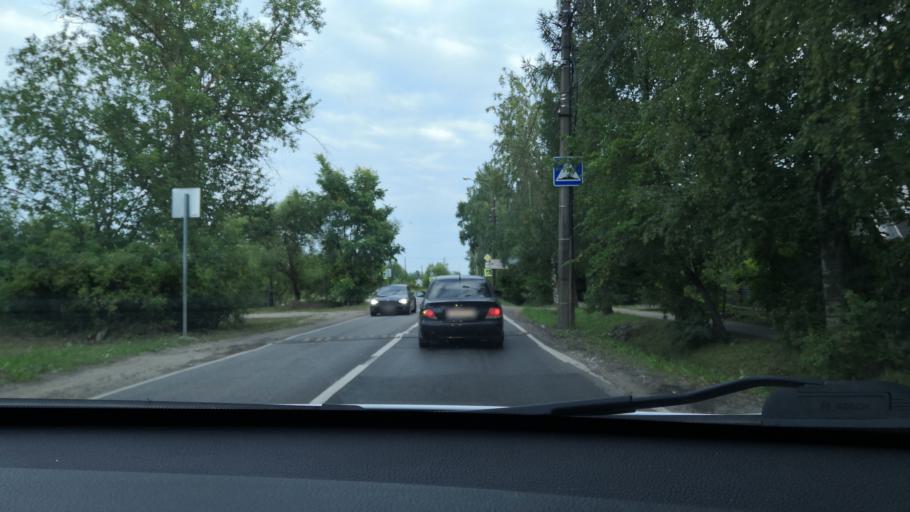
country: RU
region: St.-Petersburg
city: Pushkin
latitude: 59.6964
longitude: 30.4120
